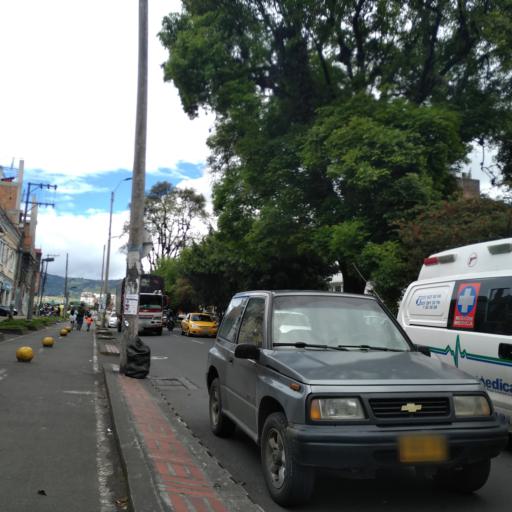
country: CO
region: Narino
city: Pasto
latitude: 1.2131
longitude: -77.2746
